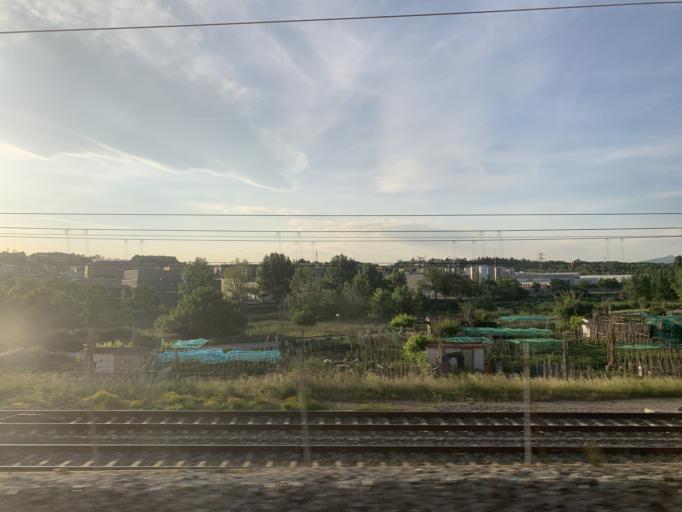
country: ES
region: Catalonia
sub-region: Provincia de Barcelona
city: Montmelo
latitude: 41.5531
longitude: 2.2563
